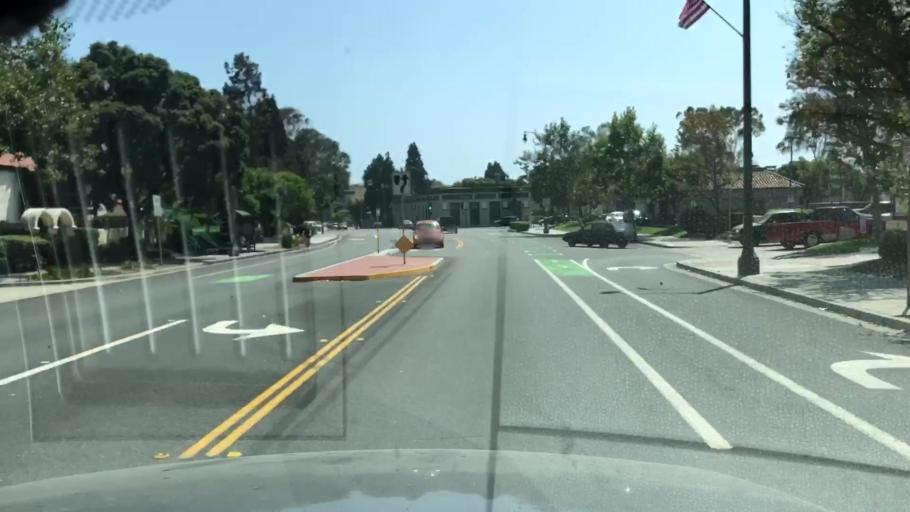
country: US
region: California
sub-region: Ventura County
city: Ventura
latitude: 34.2822
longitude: -119.3006
